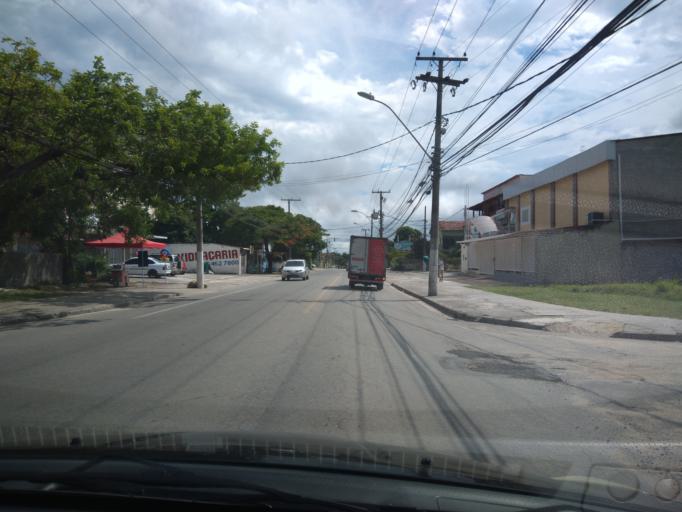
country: BR
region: Rio de Janeiro
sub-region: Niteroi
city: Niteroi
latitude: -22.9344
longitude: -43.0220
